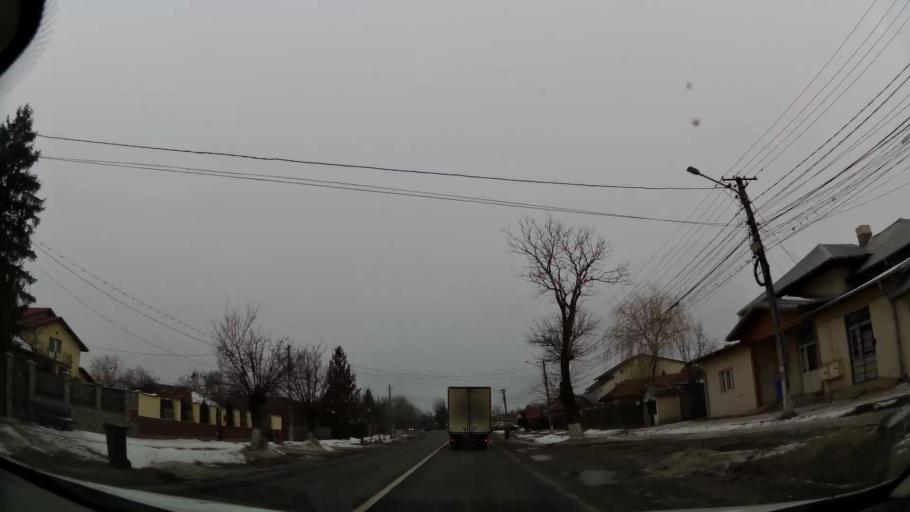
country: RO
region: Dambovita
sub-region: Comuna Tartasesti
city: Baldana
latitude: 44.6119
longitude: 25.7664
